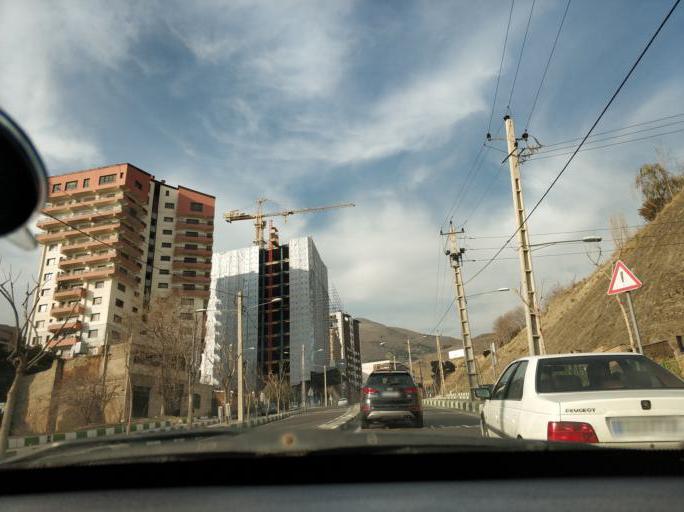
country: IR
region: Tehran
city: Tajrish
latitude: 35.8127
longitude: 51.4850
